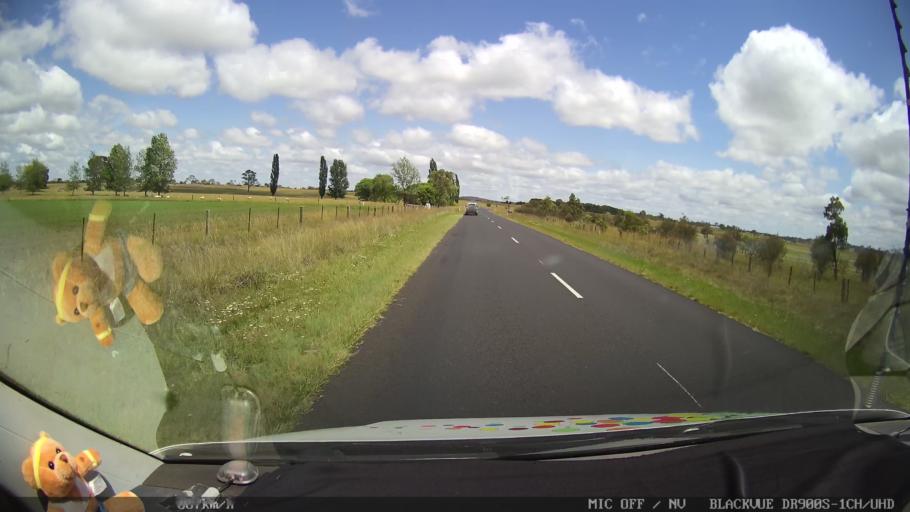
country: AU
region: New South Wales
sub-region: Glen Innes Severn
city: Glen Innes
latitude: -29.6830
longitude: 151.7005
